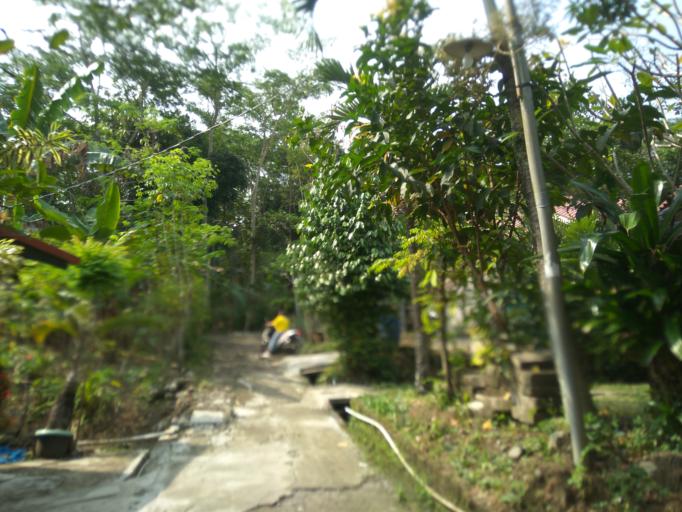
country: ID
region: Central Java
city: Semarang
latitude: -7.0368
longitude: 110.4086
